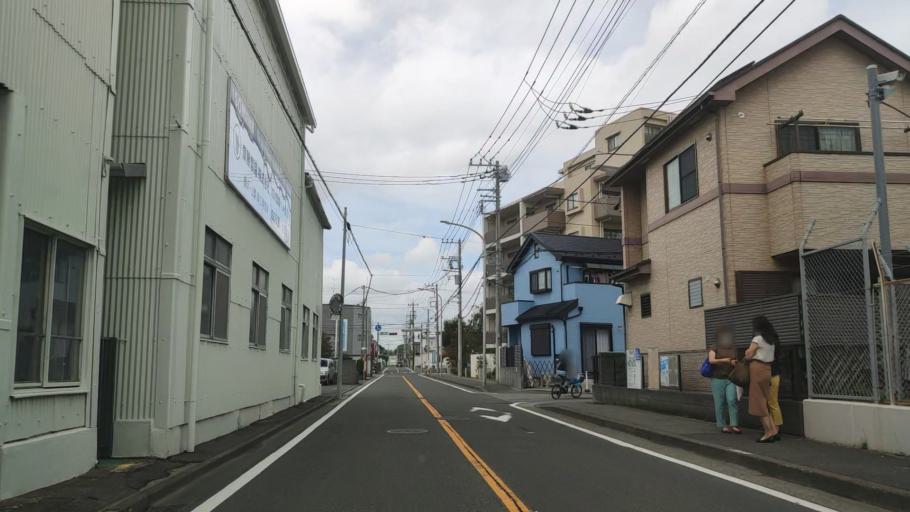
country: JP
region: Kanagawa
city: Minami-rinkan
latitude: 35.4776
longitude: 139.4756
